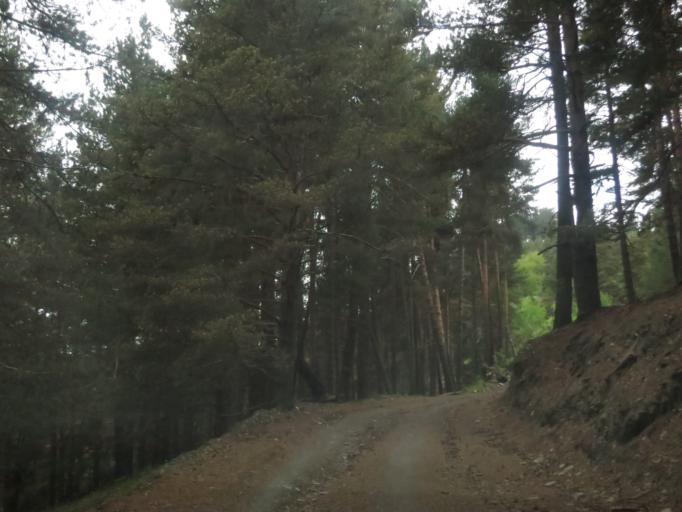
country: RU
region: Chechnya
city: Itum-Kali
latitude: 42.3659
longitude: 45.6522
